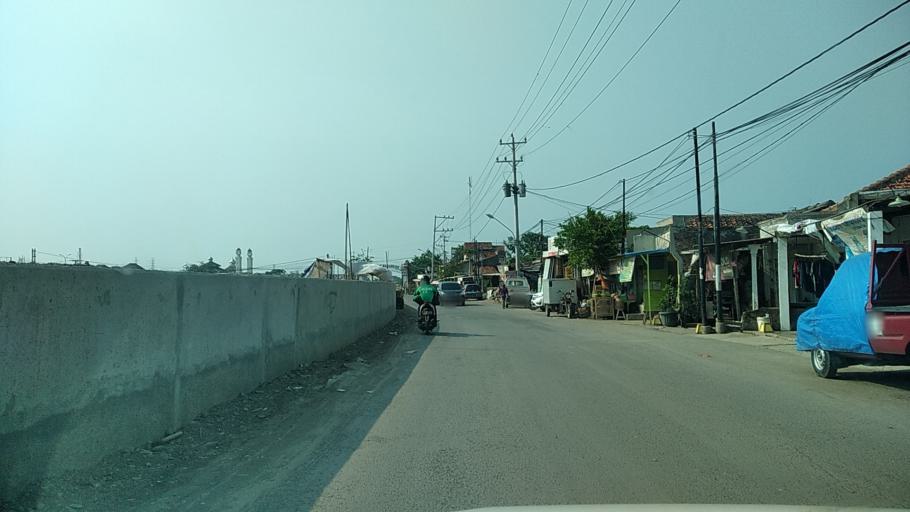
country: ID
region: Central Java
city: Semarang
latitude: -6.9613
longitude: 110.4435
